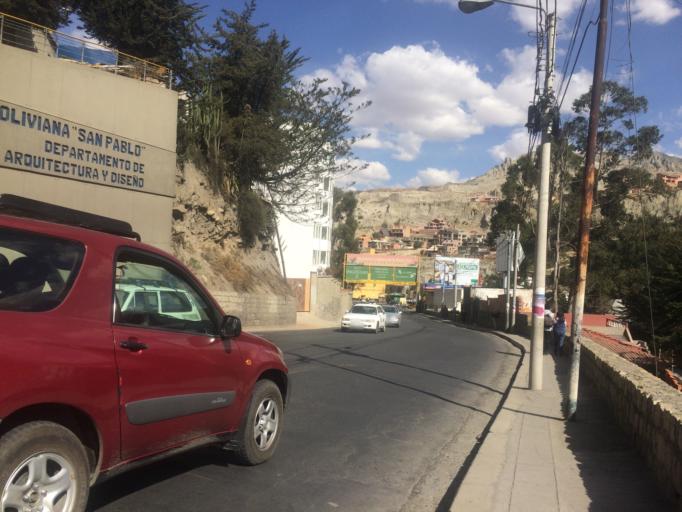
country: BO
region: La Paz
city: La Paz
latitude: -16.5207
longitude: -68.1149
